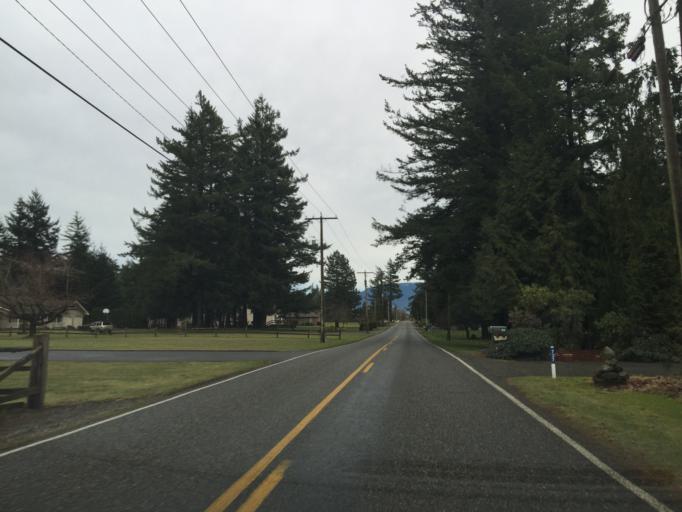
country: US
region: Washington
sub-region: Whatcom County
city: Lynden
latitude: 48.9099
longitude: -122.4520
